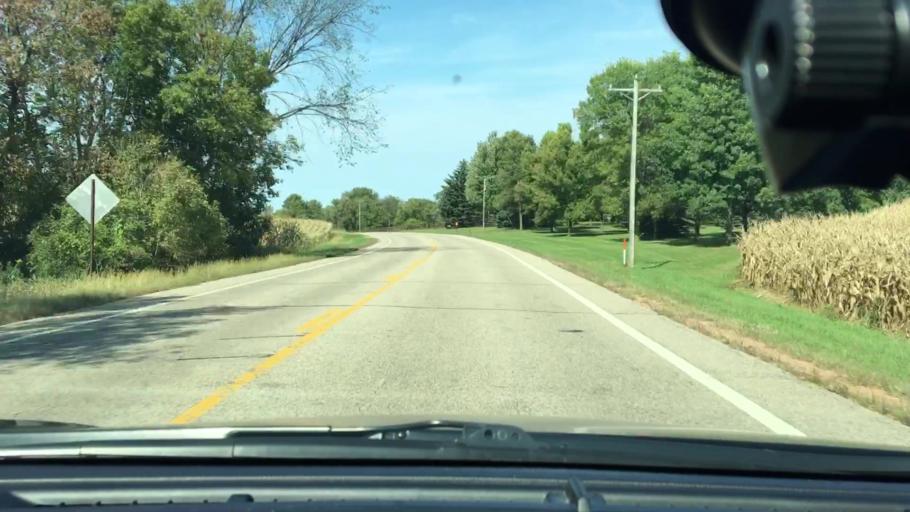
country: US
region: Minnesota
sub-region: Hennepin County
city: Corcoran
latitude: 45.0993
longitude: -93.5534
